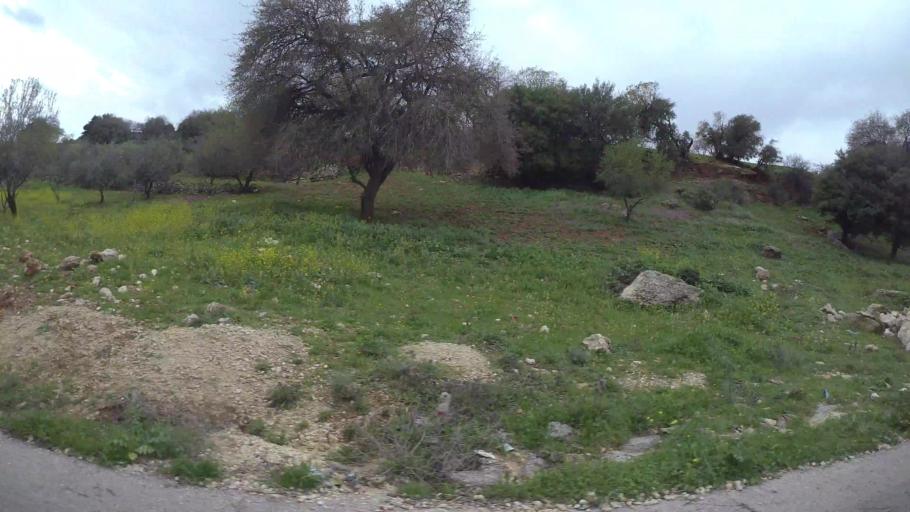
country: JO
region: Amman
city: Wadi as Sir
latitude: 31.9547
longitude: 35.8127
